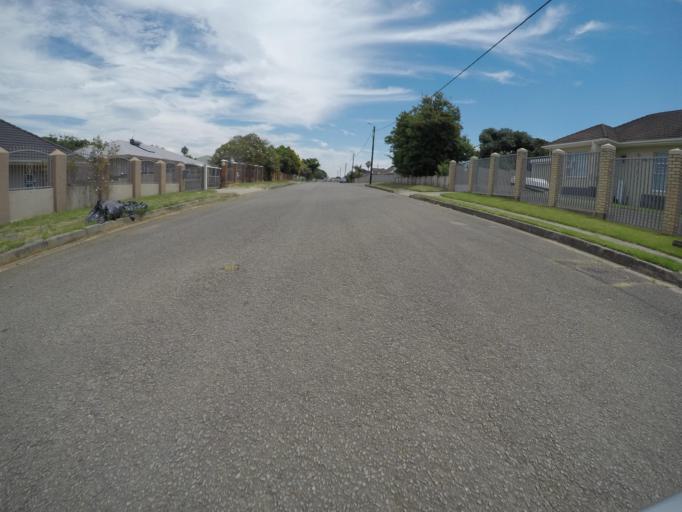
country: ZA
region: Eastern Cape
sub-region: Buffalo City Metropolitan Municipality
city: East London
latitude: -33.0381
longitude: 27.8512
